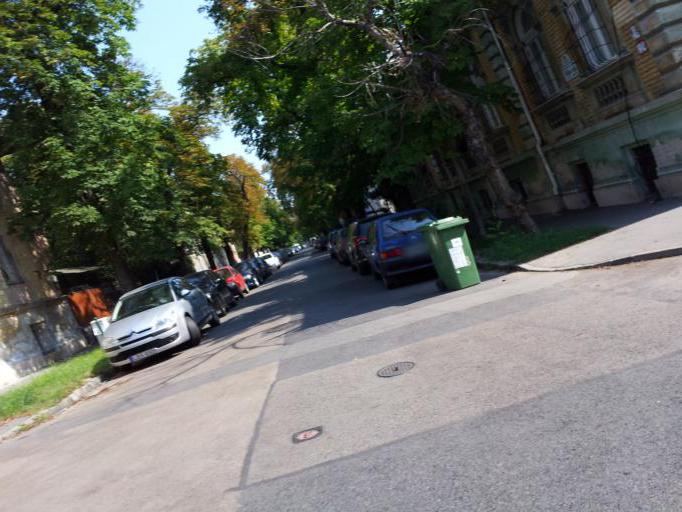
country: HU
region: Budapest
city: Budapest VIII. keruelet
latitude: 47.4803
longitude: 19.1004
